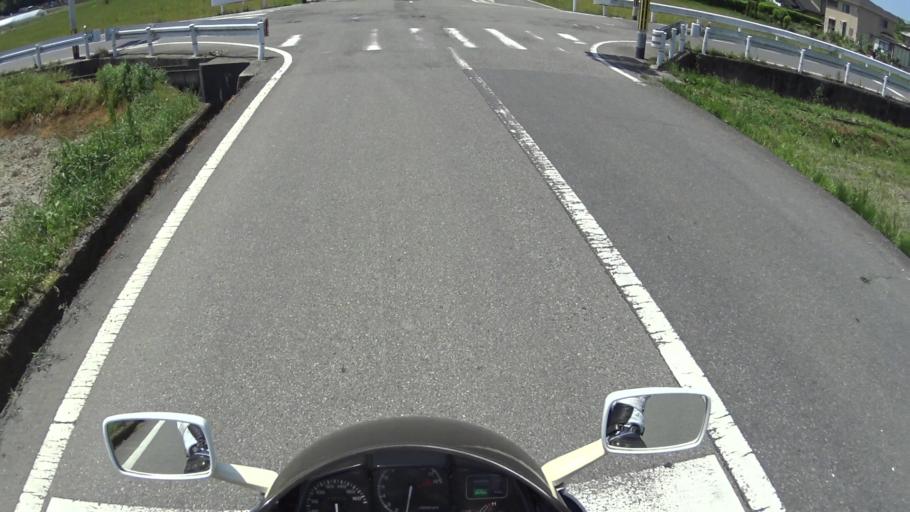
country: JP
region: Kyoto
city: Kameoka
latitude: 35.0771
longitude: 135.5502
